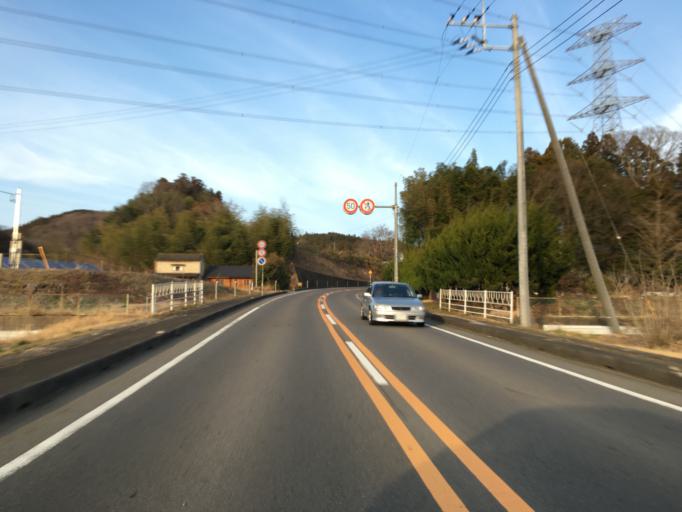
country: JP
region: Ibaraki
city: Daigo
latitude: 36.8181
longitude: 140.3711
